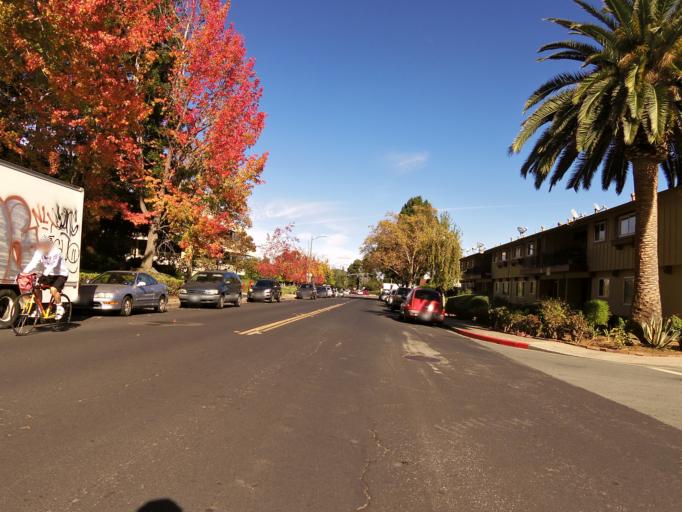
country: US
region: California
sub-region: Santa Clara County
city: Mountain View
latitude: 37.3926
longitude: -122.0990
